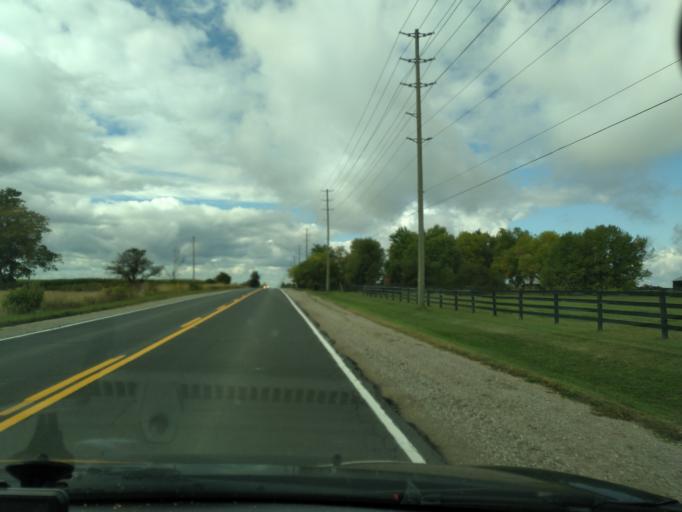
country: CA
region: Ontario
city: Innisfil
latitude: 44.2812
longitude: -79.6969
